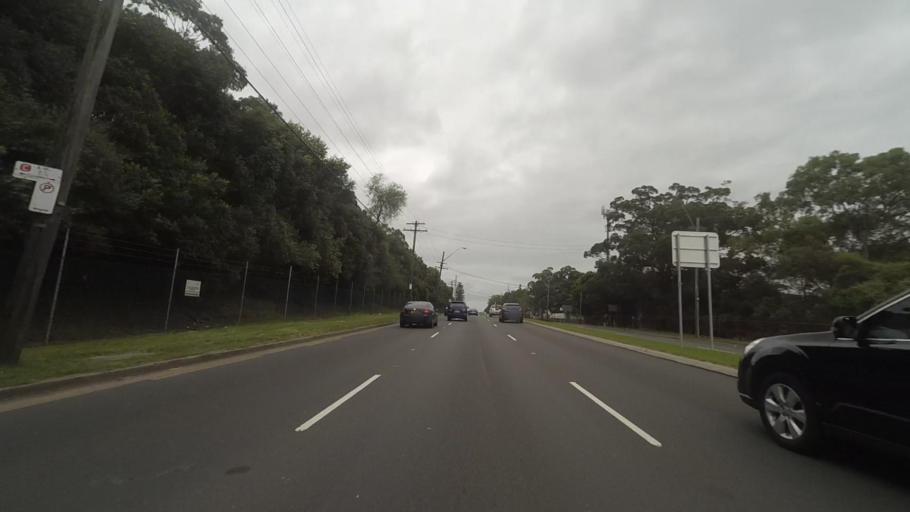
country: AU
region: New South Wales
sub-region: Auburn
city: Berala
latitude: -33.8908
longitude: 151.0388
